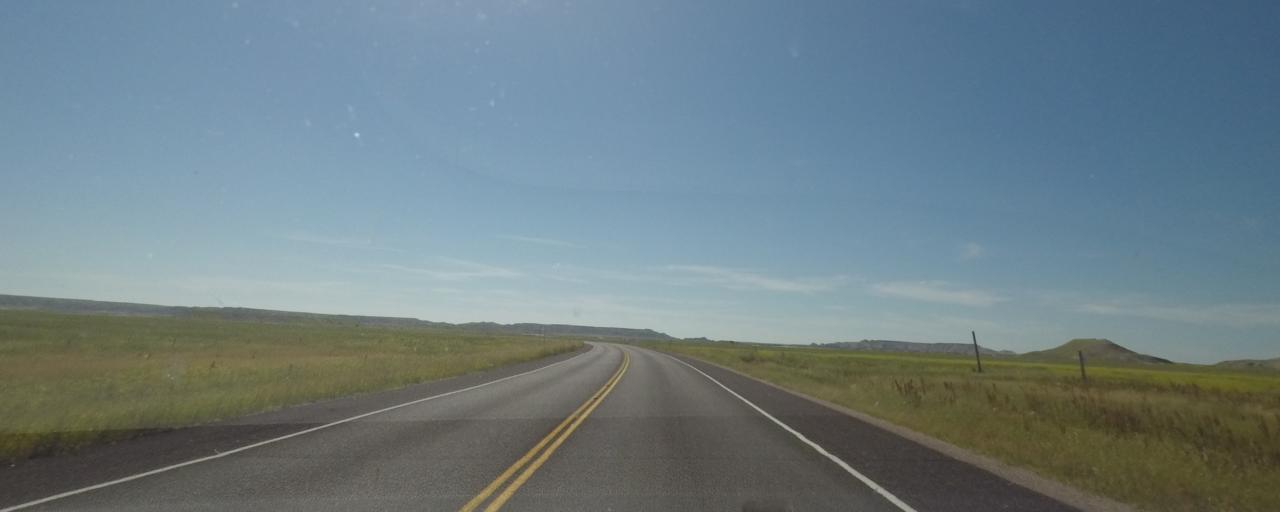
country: US
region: South Dakota
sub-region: Shannon County
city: Porcupine
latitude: 43.7804
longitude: -102.5500
